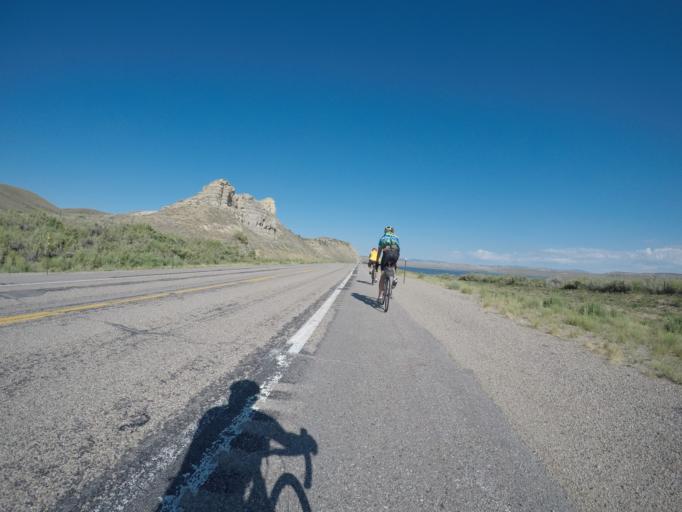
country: US
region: Wyoming
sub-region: Sublette County
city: Marbleton
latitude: 42.1115
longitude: -110.1440
